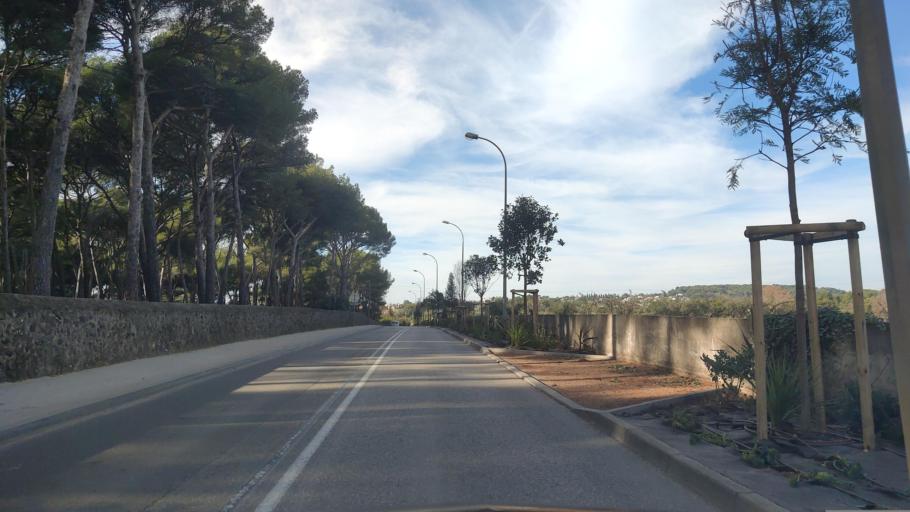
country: FR
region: Provence-Alpes-Cote d'Azur
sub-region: Departement du Var
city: Sanary-sur-Mer
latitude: 43.1273
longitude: 5.8133
